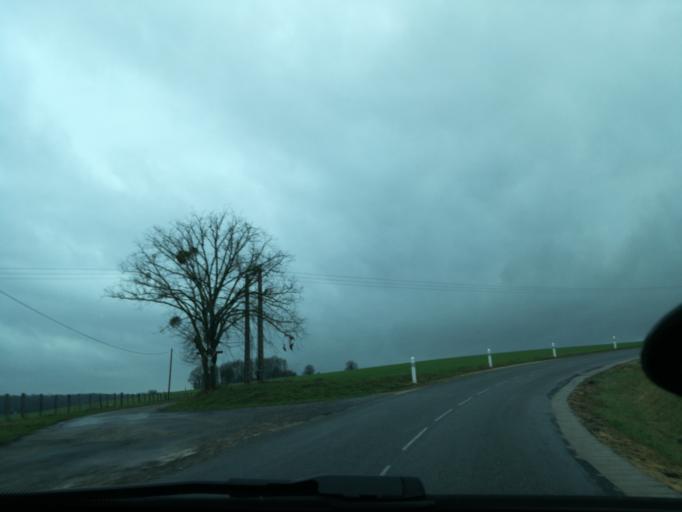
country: FR
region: Lorraine
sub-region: Departement de la Meuse
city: Fains-Veel
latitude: 48.8720
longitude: 5.0816
